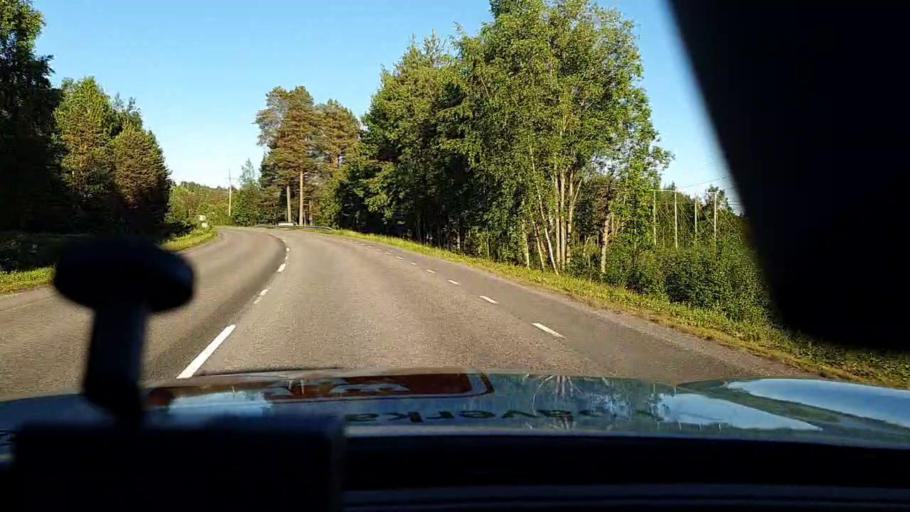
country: SE
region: Norrbotten
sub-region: Lulea Kommun
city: Lulea
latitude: 65.6077
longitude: 22.1698
